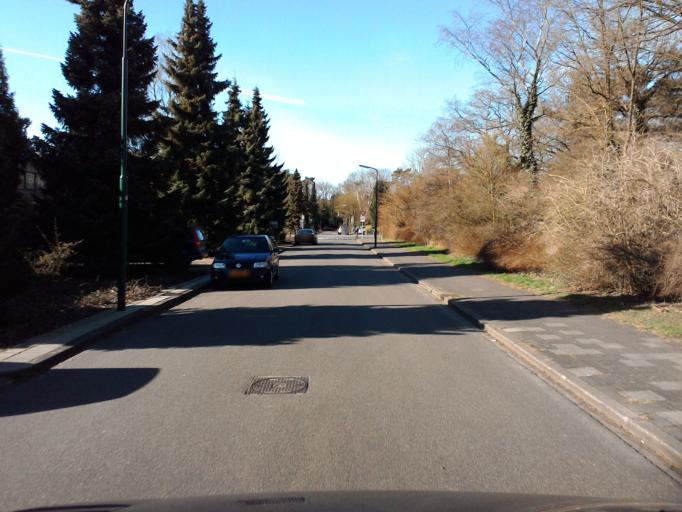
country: NL
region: Utrecht
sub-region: Gemeente De Bilt
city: De Bilt
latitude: 52.1290
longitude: 5.2149
